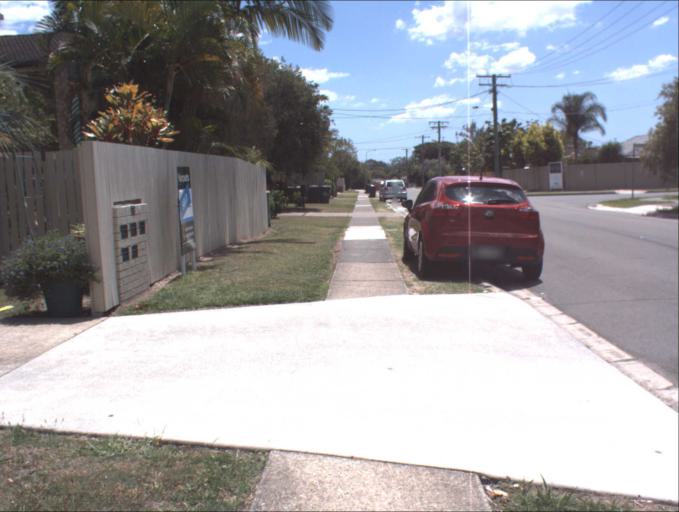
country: AU
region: Queensland
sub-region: Logan
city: Windaroo
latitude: -27.7304
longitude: 153.2094
